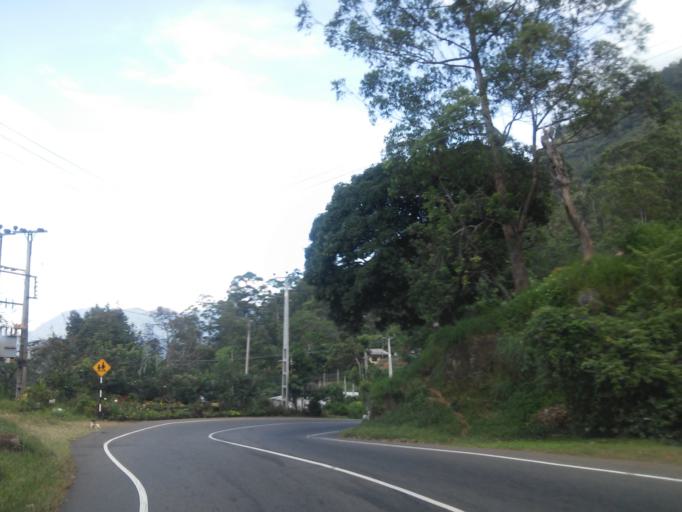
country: LK
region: Uva
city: Haputale
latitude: 6.7628
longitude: 80.9258
